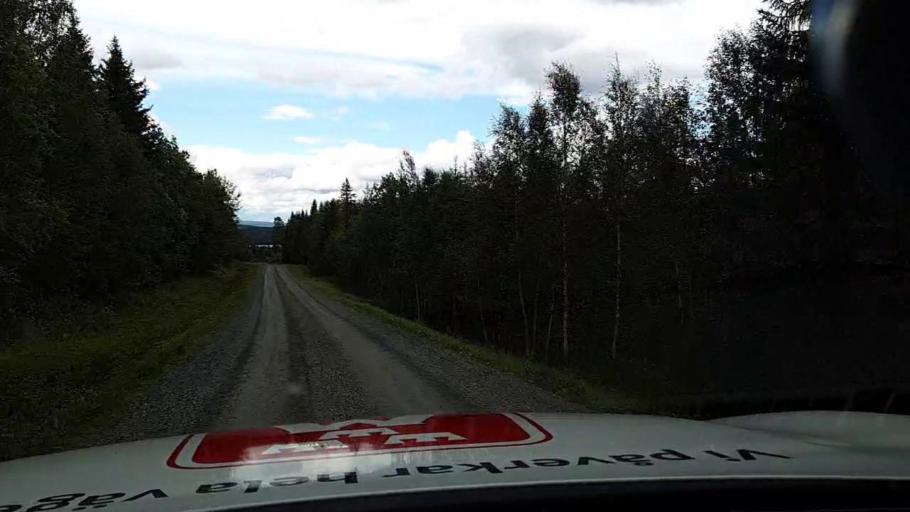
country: SE
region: Jaemtland
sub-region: Krokoms Kommun
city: Valla
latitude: 63.5235
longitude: 13.8982
